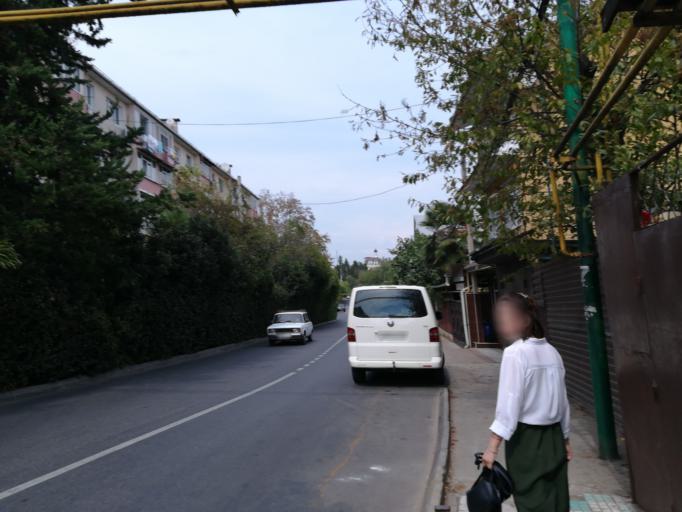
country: RU
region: Krasnodarskiy
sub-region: Sochi City
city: Sochi
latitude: 43.5928
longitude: 39.7416
